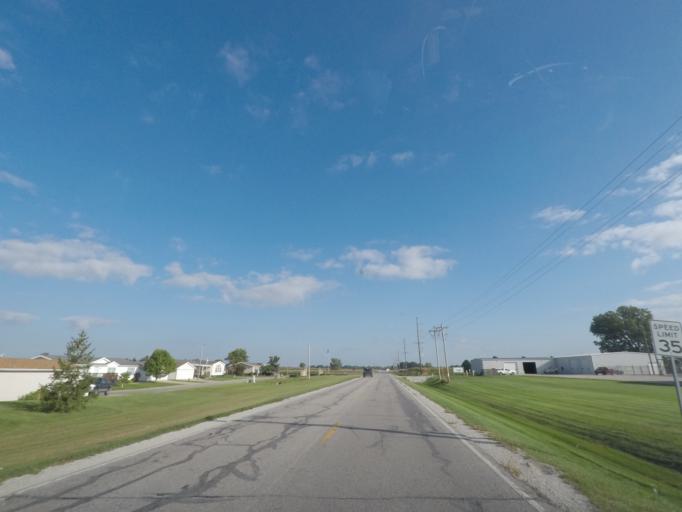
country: US
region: Iowa
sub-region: Story County
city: Nevada
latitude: 42.0011
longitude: -93.4628
